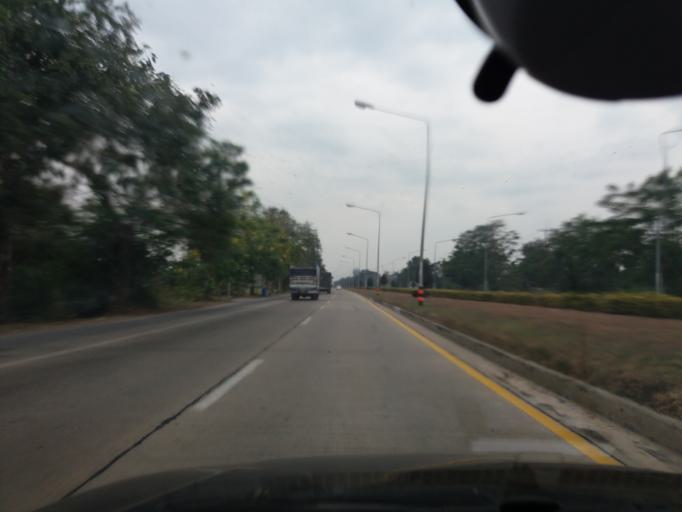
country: TH
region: Suphan Buri
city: Sam Chuk
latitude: 14.7671
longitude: 100.0929
